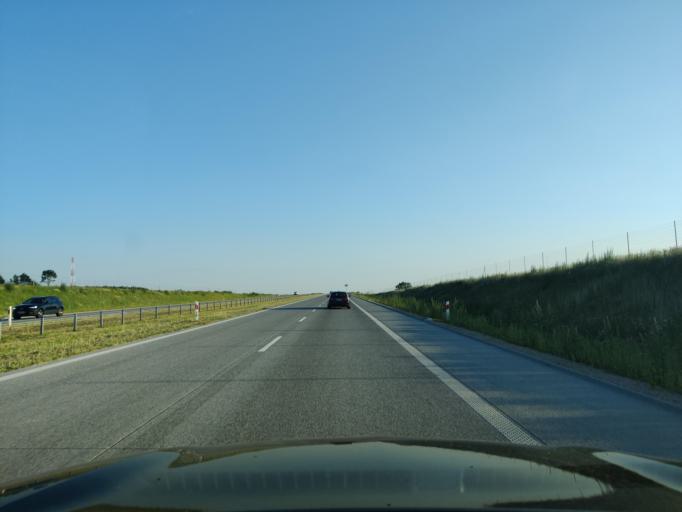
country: PL
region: Masovian Voivodeship
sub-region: Powiat mlawski
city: Wisniewo
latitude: 53.0223
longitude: 20.3431
